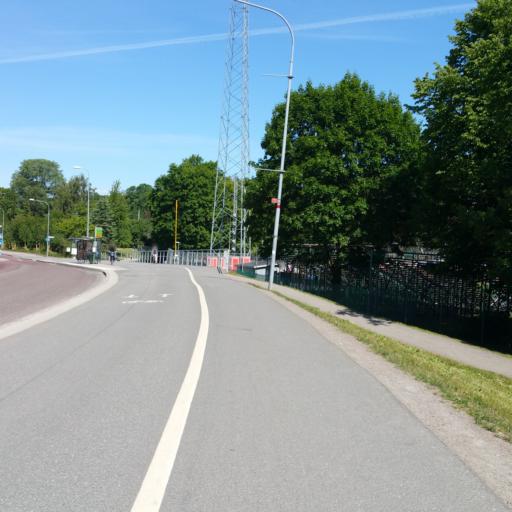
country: SE
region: Uppsala
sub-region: Uppsala Kommun
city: Uppsala
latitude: 59.8491
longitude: 17.6440
